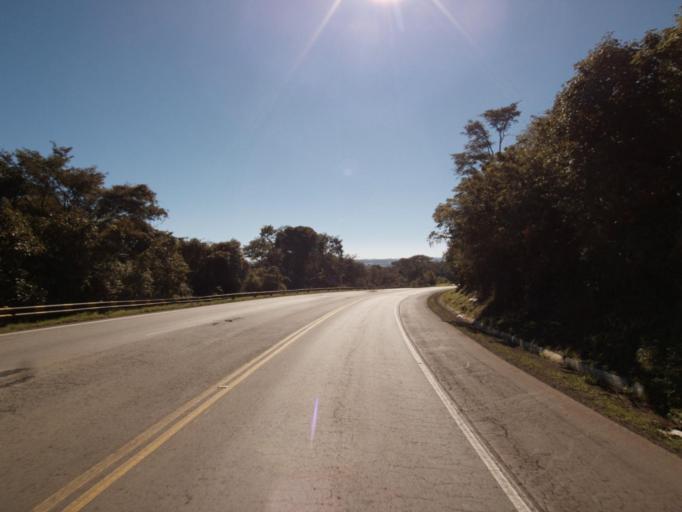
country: BR
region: Santa Catarina
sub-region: Sao Lourenco Do Oeste
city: Sao Lourenco dOeste
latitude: -26.8227
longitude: -53.1816
